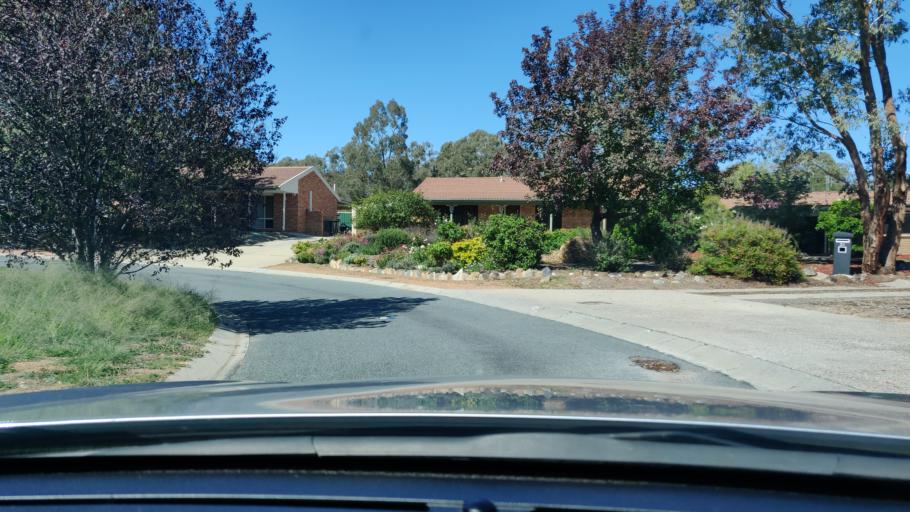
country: AU
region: Australian Capital Territory
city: Macarthur
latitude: -35.4422
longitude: 149.0970
